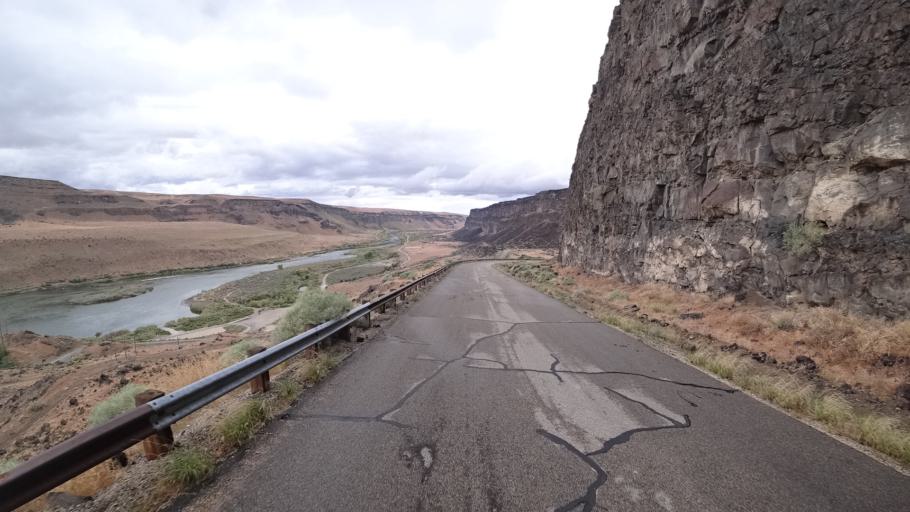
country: US
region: Idaho
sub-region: Owyhee County
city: Murphy
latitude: 43.2453
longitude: -116.3733
